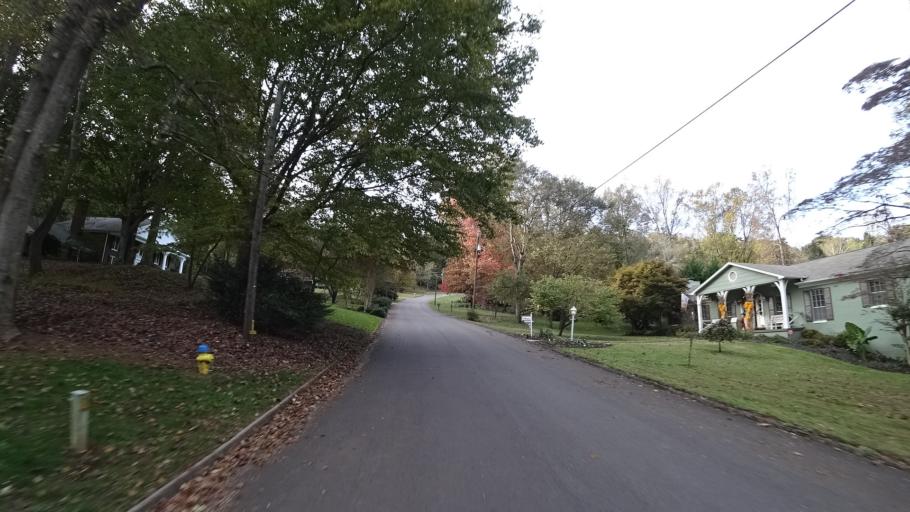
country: US
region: Tennessee
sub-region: Knox County
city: Knoxville
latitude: 35.9096
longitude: -83.9911
